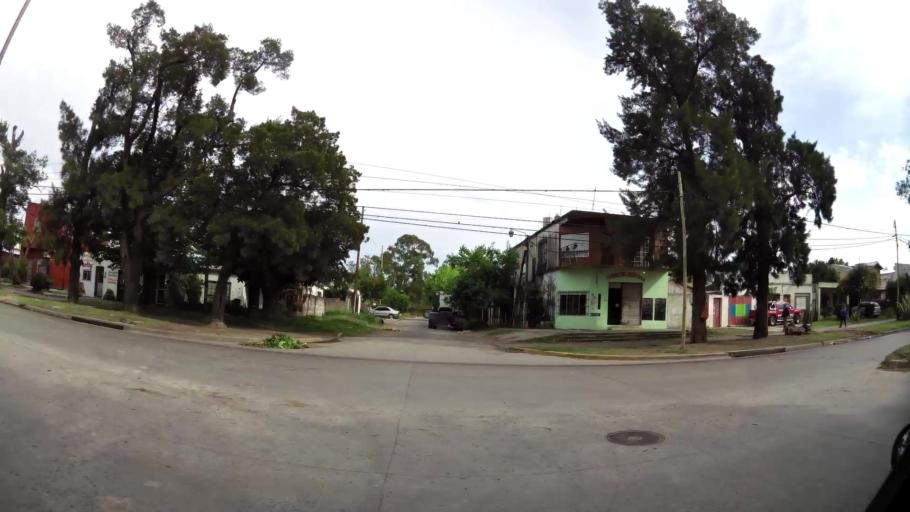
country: AR
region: Buenos Aires
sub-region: Partido de Quilmes
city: Quilmes
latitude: -34.7120
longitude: -58.2393
